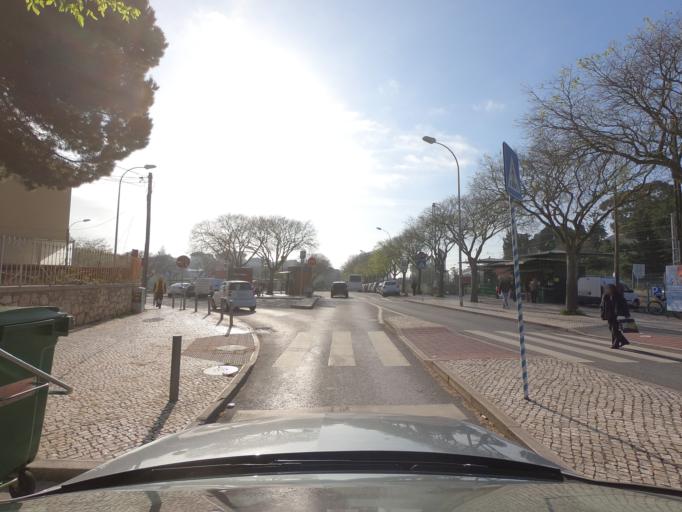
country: PT
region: Lisbon
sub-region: Oeiras
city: Carcavelos
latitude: 38.6886
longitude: -9.3178
